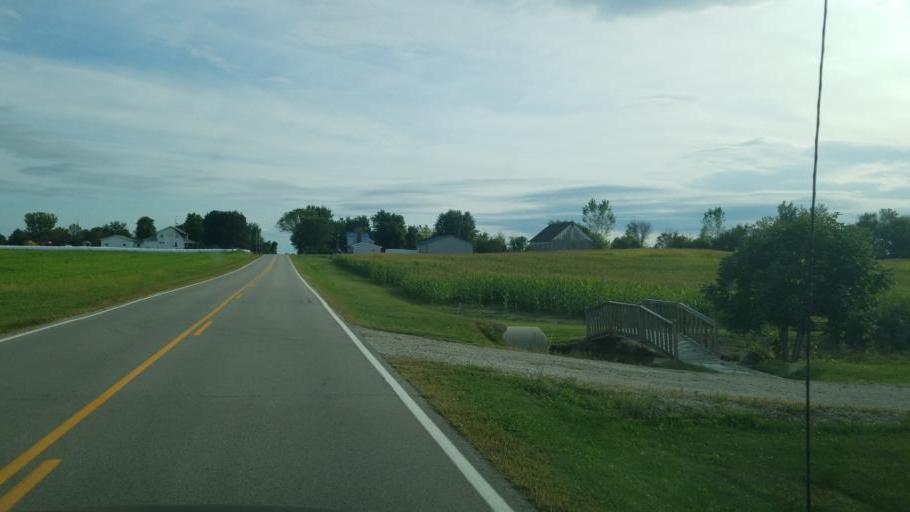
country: US
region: Ohio
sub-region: Crawford County
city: Bucyrus
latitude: 40.8991
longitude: -83.0935
